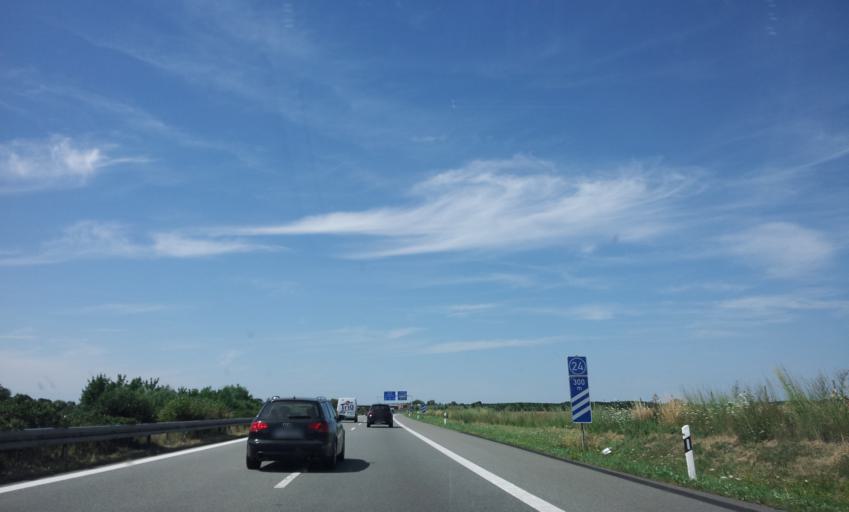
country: DE
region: Mecklenburg-Vorpommern
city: Grimmen
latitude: 54.0827
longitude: 13.1389
